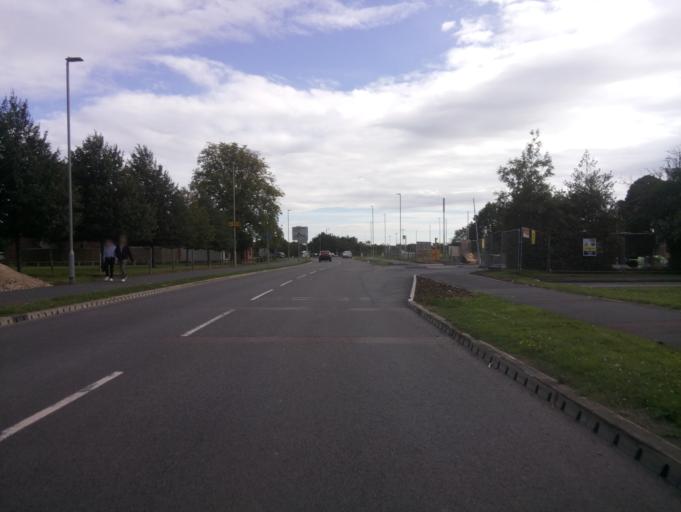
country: GB
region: England
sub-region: Gloucestershire
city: Gloucester
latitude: 51.8188
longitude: -2.2757
